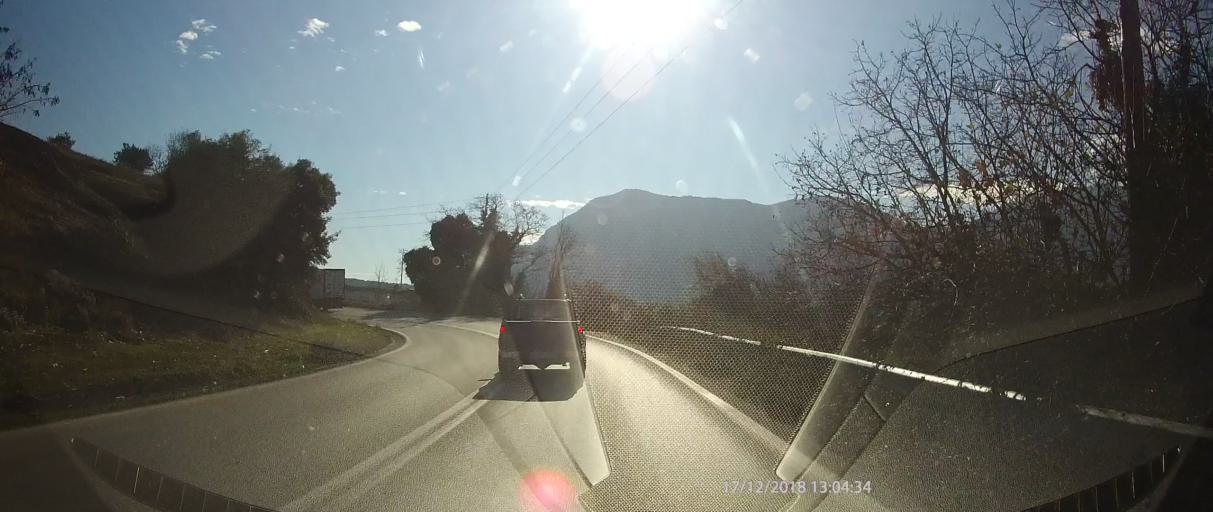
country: GR
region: Thessaly
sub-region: Trikala
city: Kastraki
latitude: 39.7041
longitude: 21.6116
